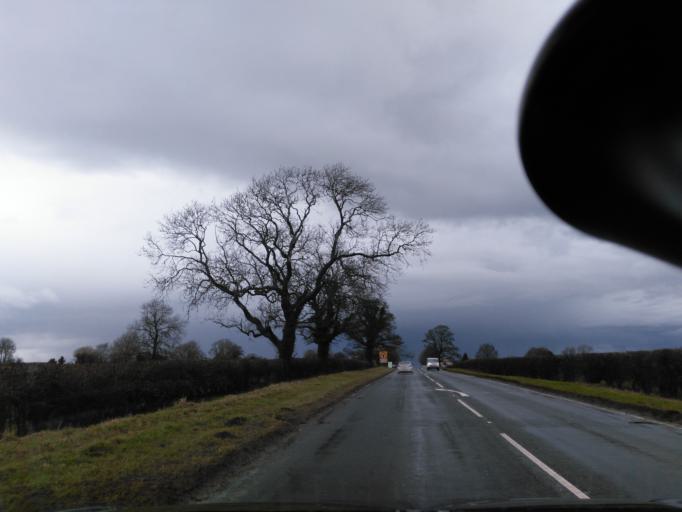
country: GB
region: England
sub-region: North Yorkshire
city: Ripon
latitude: 54.0880
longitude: -1.5301
